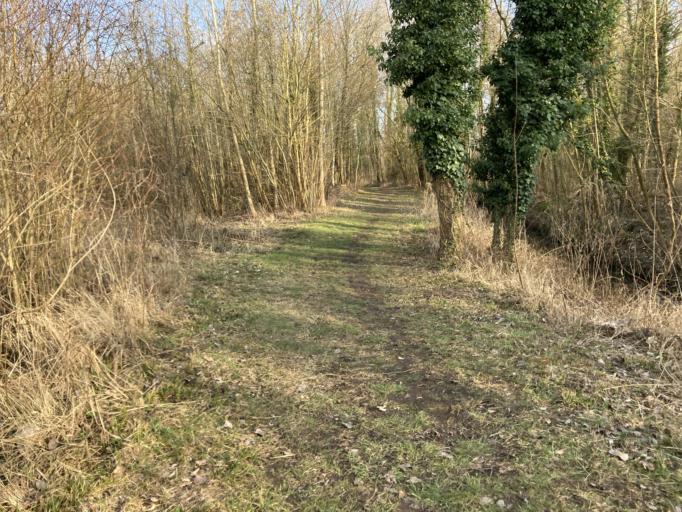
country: FR
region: Nord-Pas-de-Calais
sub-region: Departement du Pas-de-Calais
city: Annequin
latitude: 50.5189
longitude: 2.7073
